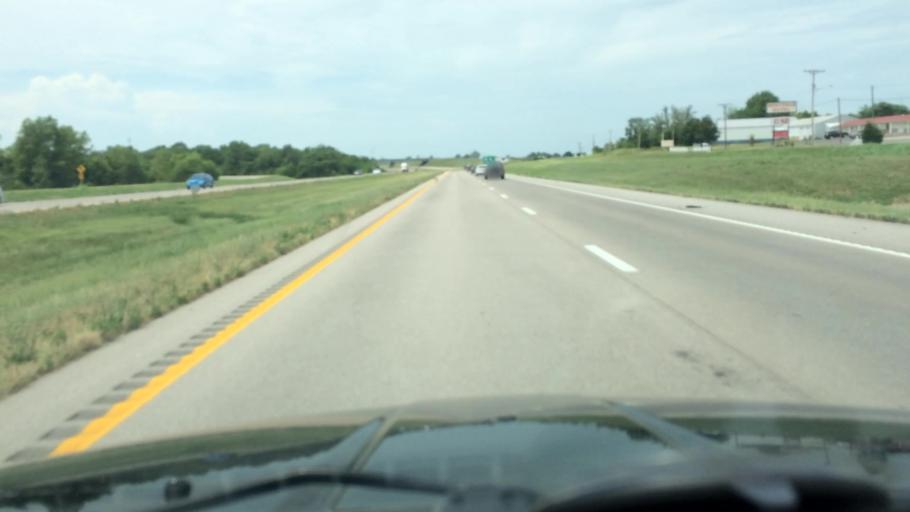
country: US
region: Missouri
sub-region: Polk County
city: Bolivar
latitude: 37.5680
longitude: -93.3949
